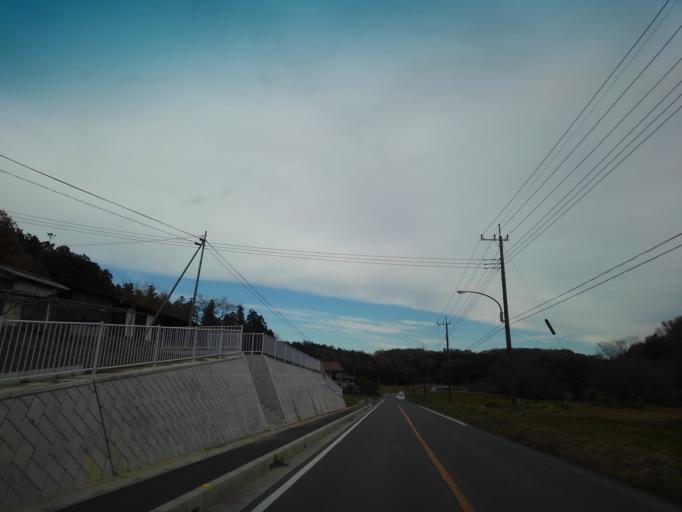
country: JP
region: Saitama
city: Morohongo
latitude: 35.9841
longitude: 139.3068
